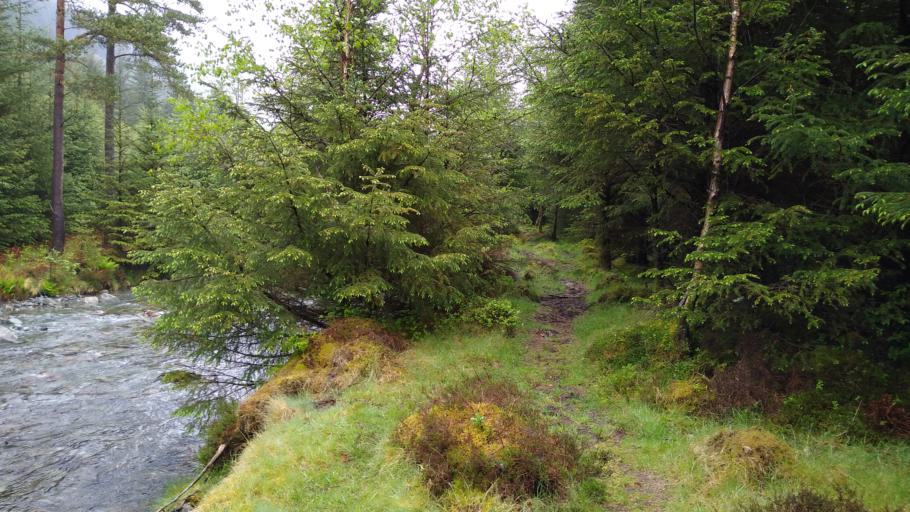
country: GB
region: England
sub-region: Cumbria
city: Cockermouth
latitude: 54.5124
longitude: -3.3028
